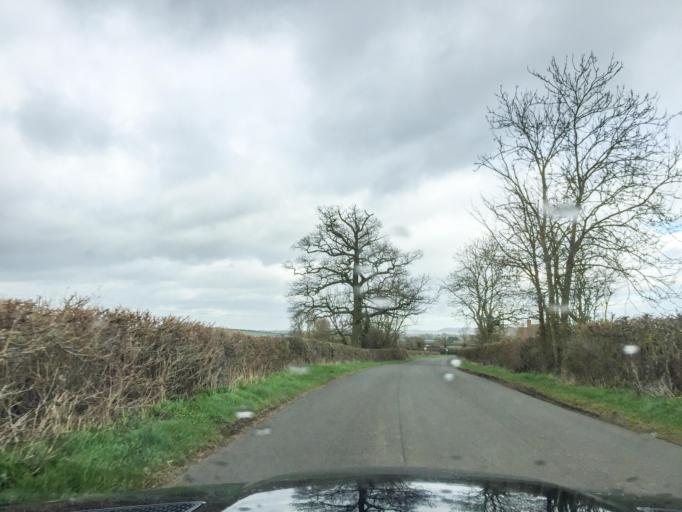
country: GB
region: England
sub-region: Warwickshire
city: Shipston on Stour
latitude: 52.0943
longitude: -1.5855
